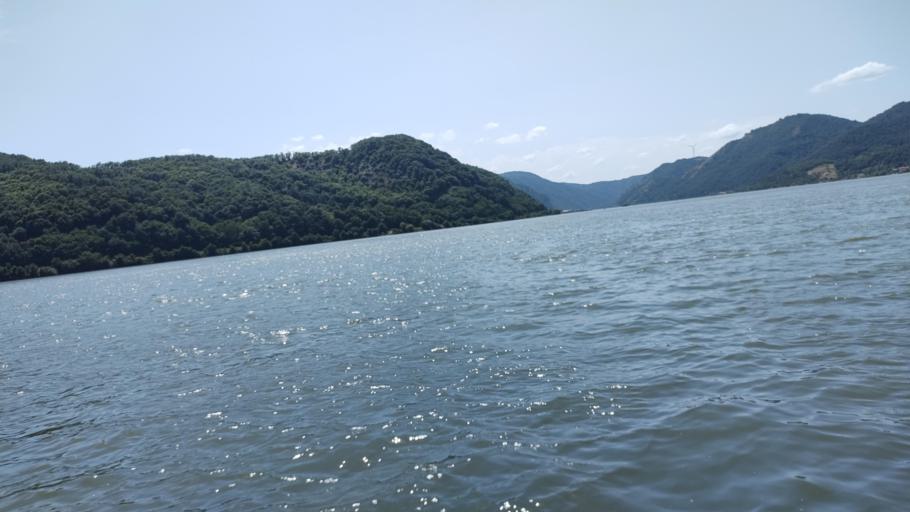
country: RS
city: Radenka
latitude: 44.6598
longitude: 21.7861
